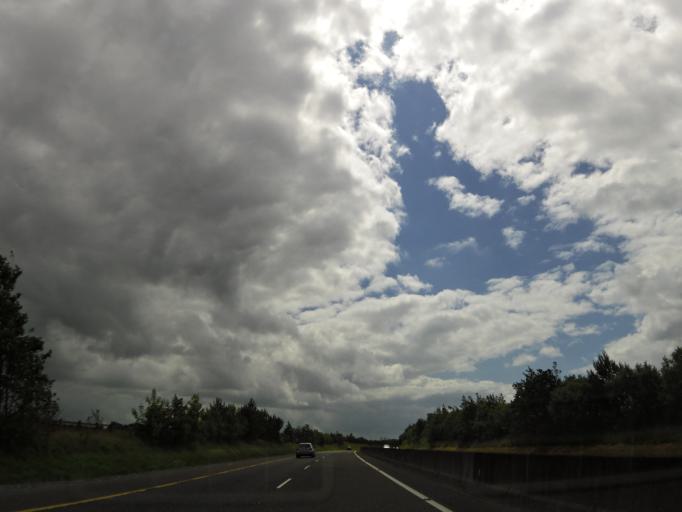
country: IE
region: Munster
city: Cashel
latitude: 52.5302
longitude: -7.8589
